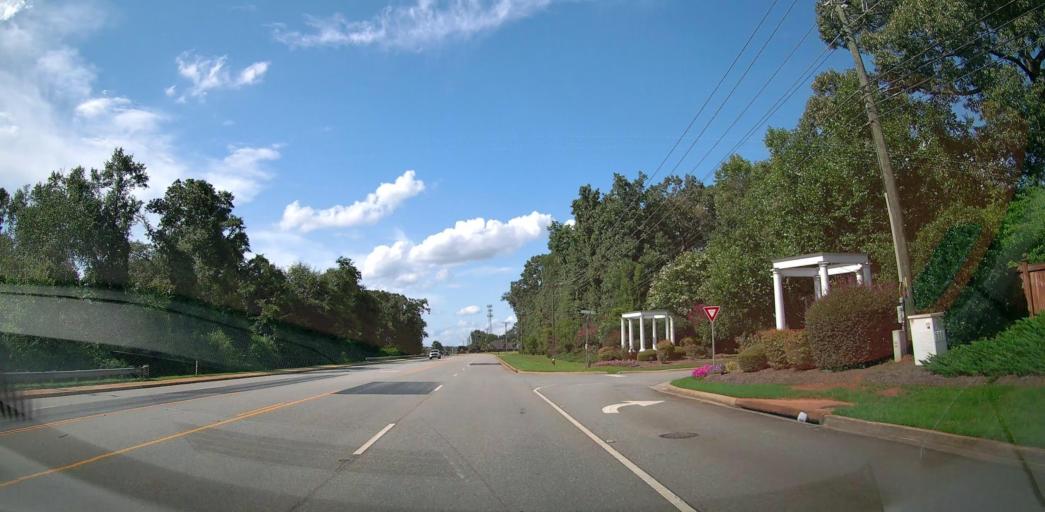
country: US
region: Georgia
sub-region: Houston County
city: Centerville
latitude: 32.5420
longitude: -83.6908
